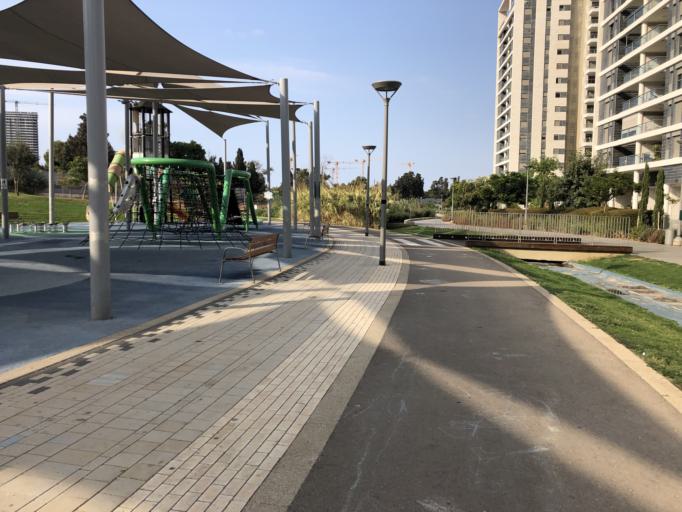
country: IL
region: Tel Aviv
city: Giv`at Shemu'el
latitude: 32.0555
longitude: 34.8452
